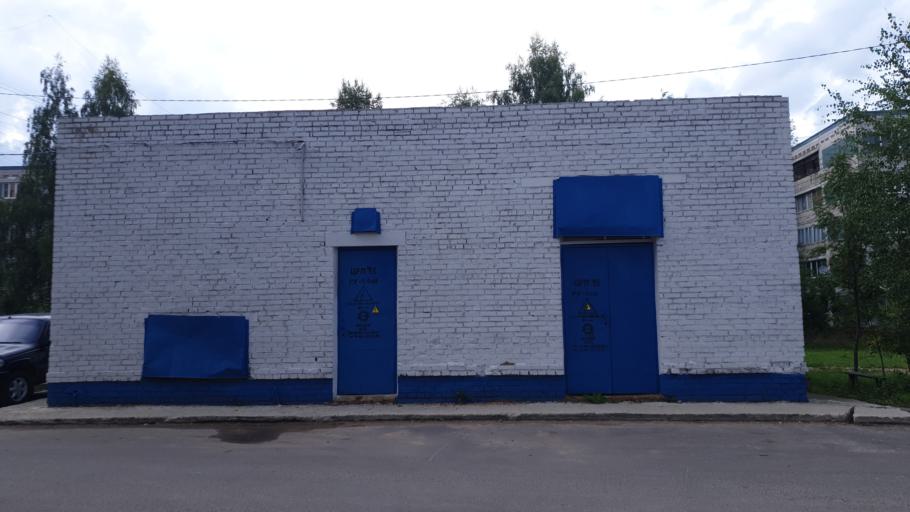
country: RU
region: Moskovskaya
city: Yakhroma
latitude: 56.2843
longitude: 37.4904
